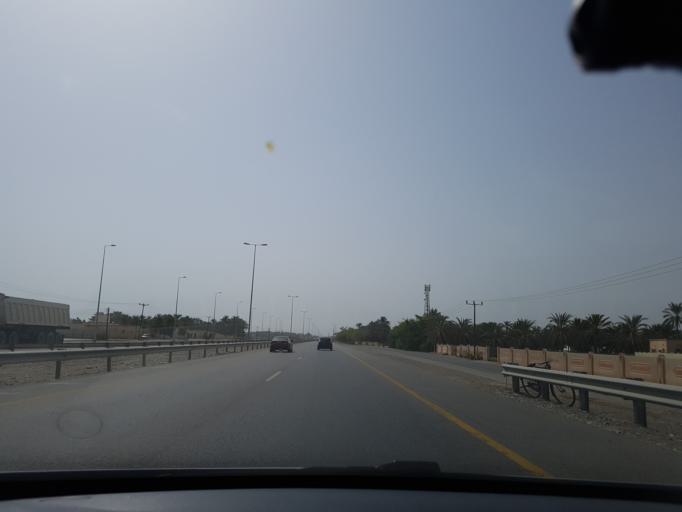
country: OM
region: Al Batinah
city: Al Khaburah
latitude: 24.0022
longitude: 57.0564
